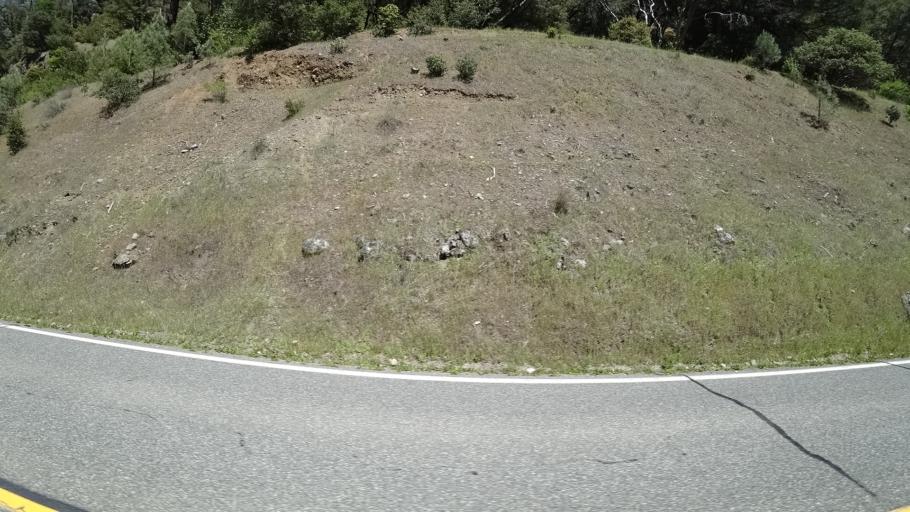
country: US
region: California
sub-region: Trinity County
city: Hayfork
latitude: 40.7640
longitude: -123.2908
